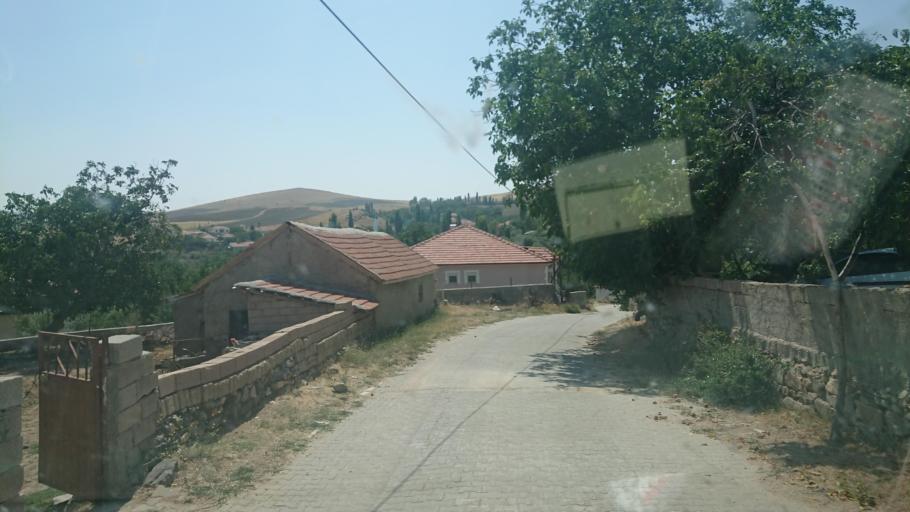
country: TR
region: Aksaray
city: Agacoren
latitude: 38.8224
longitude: 33.9575
